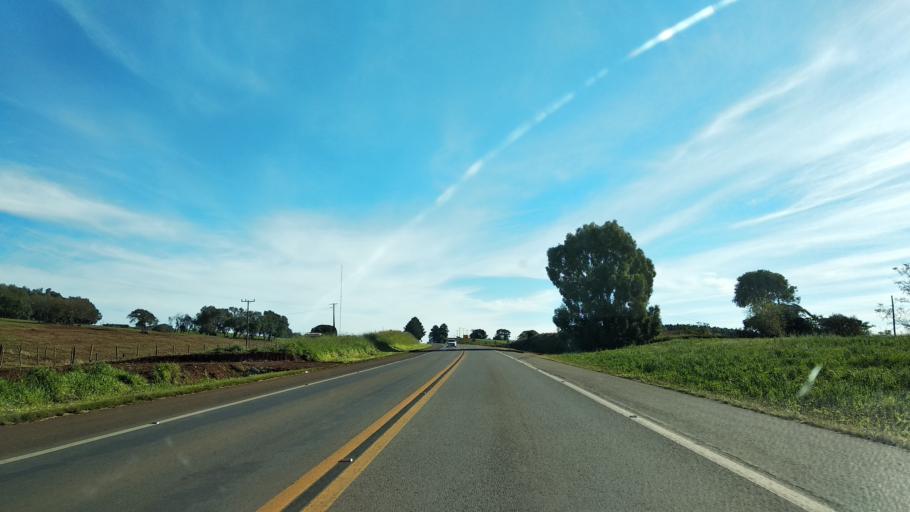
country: BR
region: Santa Catarina
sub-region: Celso Ramos
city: Celso Ramos
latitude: -27.5273
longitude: -51.3781
